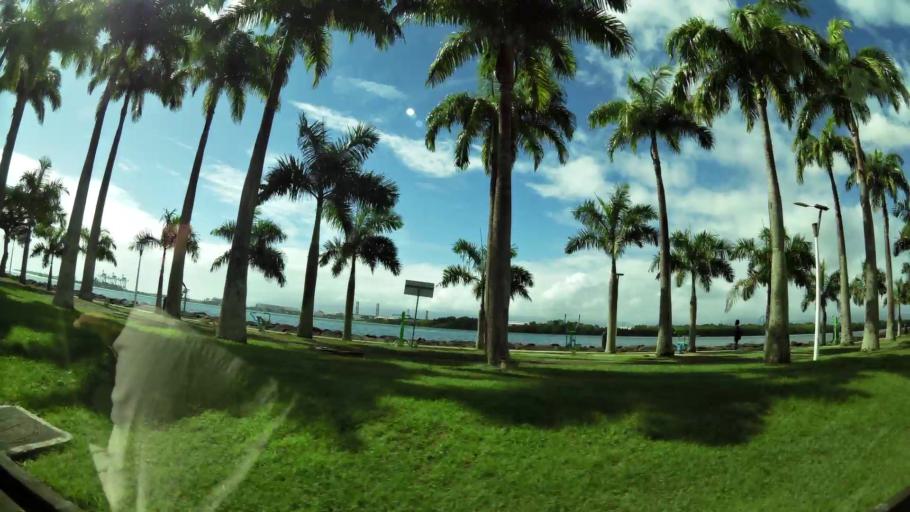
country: GP
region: Guadeloupe
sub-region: Guadeloupe
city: Pointe-a-Pitre
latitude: 16.2469
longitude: -61.5444
